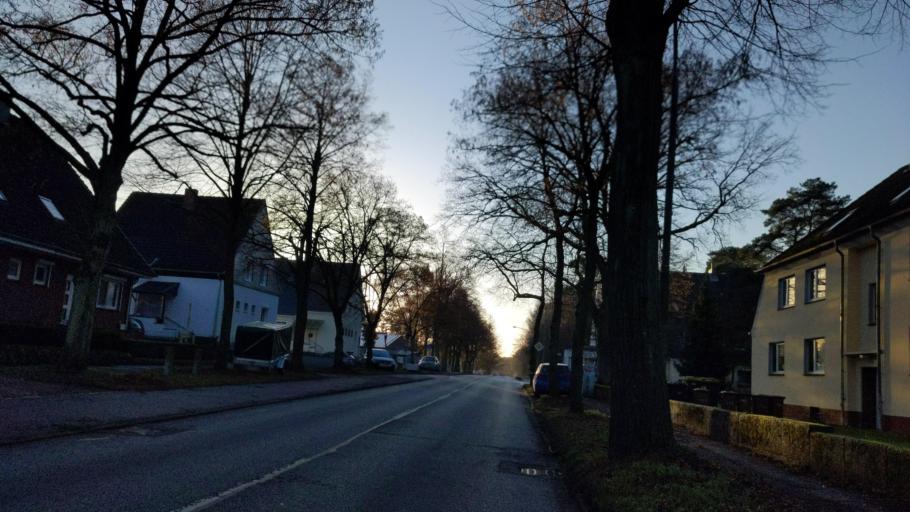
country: DE
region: Mecklenburg-Vorpommern
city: Selmsdorf
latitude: 53.8820
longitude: 10.7815
